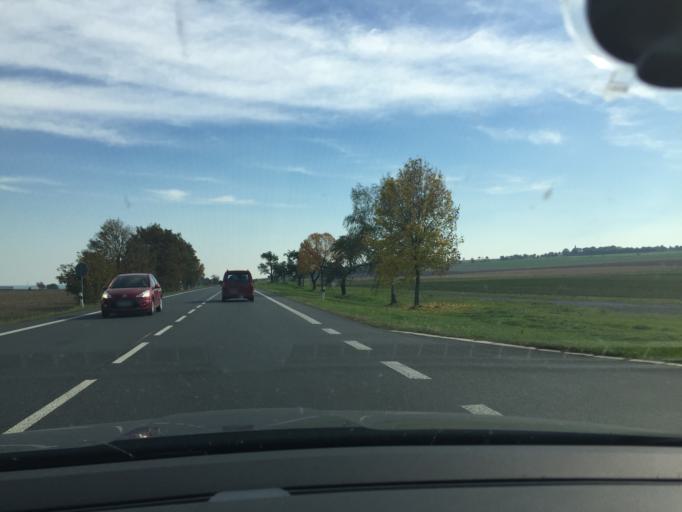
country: CZ
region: Central Bohemia
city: Velim
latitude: 50.0394
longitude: 15.1112
